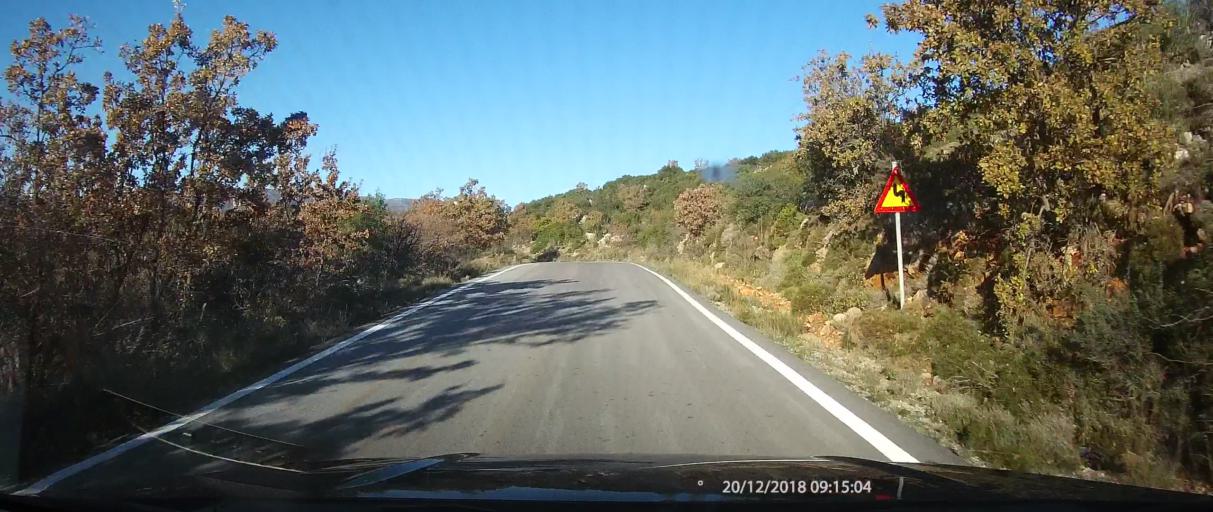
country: GR
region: Peloponnese
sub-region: Nomos Lakonias
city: Sykea
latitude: 36.9030
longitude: 22.9810
